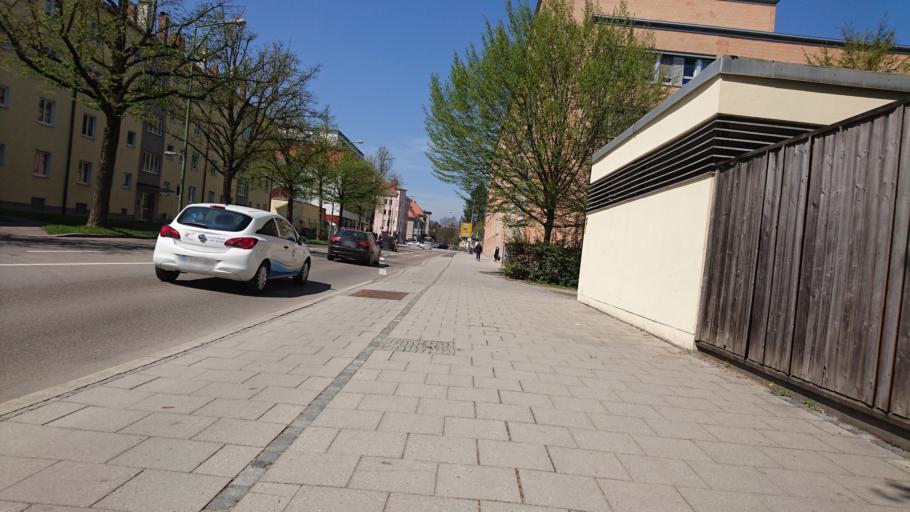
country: DE
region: Bavaria
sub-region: Swabia
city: Augsburg
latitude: 48.3547
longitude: 10.8873
